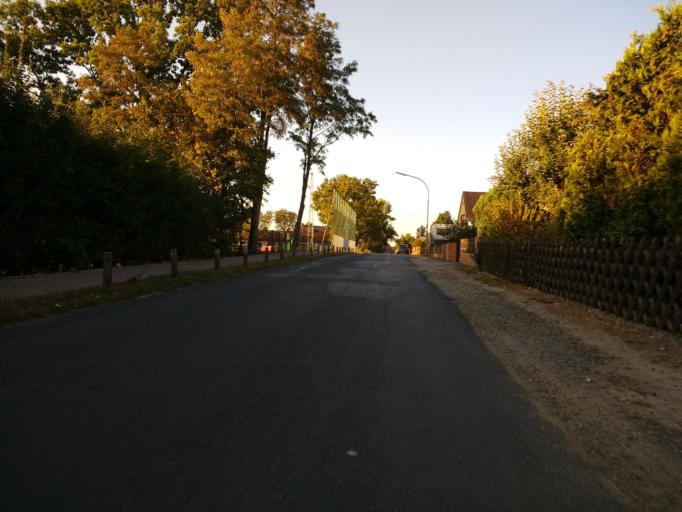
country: DE
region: Lower Saxony
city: Gifhorn
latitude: 52.5005
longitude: 10.5362
